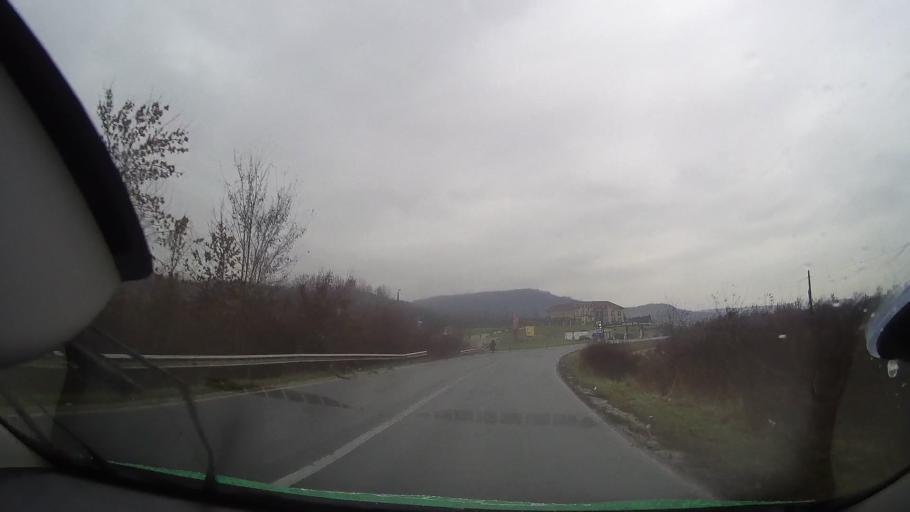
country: RO
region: Bihor
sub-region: Comuna Sambata
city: Sambata
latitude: 46.7906
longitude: 22.2044
